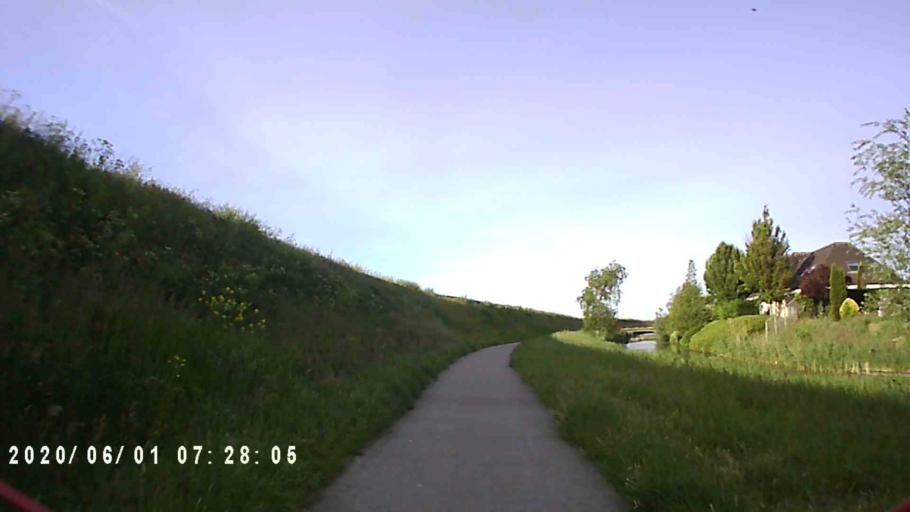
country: NL
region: Friesland
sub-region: Gemeente Dongeradeel
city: Dokkum
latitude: 53.3156
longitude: 6.0159
